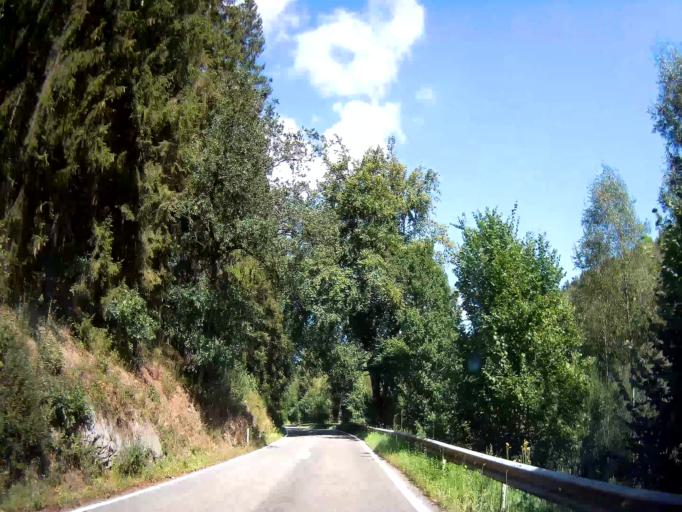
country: BE
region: Wallonia
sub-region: Province du Luxembourg
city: Bertogne
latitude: 50.0946
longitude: 5.6746
